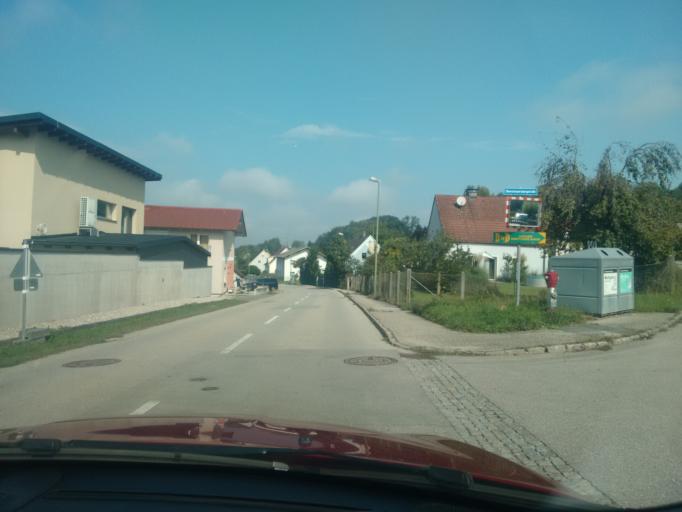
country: AT
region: Upper Austria
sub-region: Wels-Land
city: Steinhaus
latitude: 48.1298
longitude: 14.0109
